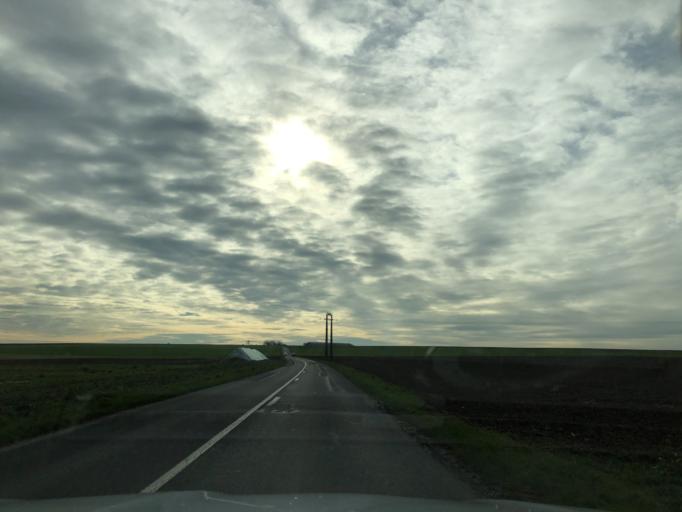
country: FR
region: Lower Normandy
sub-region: Departement du Calvados
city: Hermanville-sur-Mer
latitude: 49.2754
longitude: -0.3175
